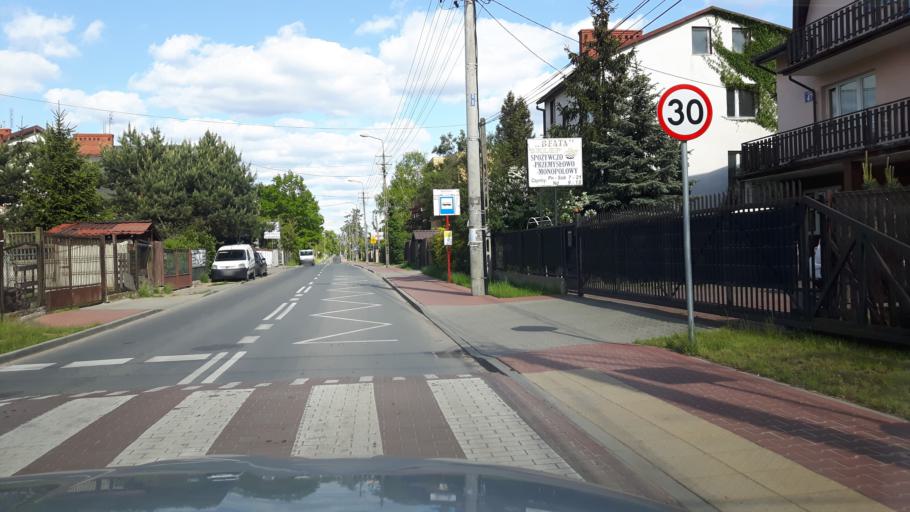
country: PL
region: Masovian Voivodeship
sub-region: Powiat wolominski
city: Marki
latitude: 52.3143
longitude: 21.1328
